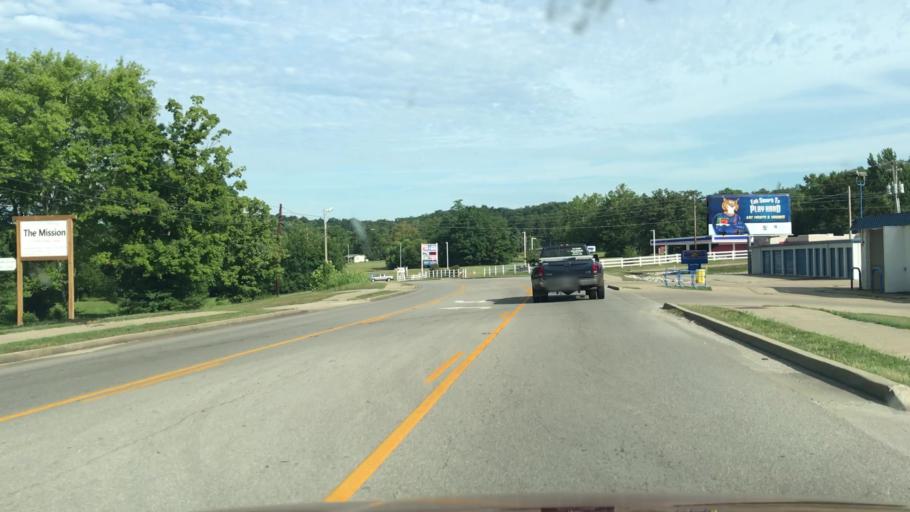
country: US
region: Kentucky
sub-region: Edmonson County
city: Brownsville
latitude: 37.1893
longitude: -86.2542
